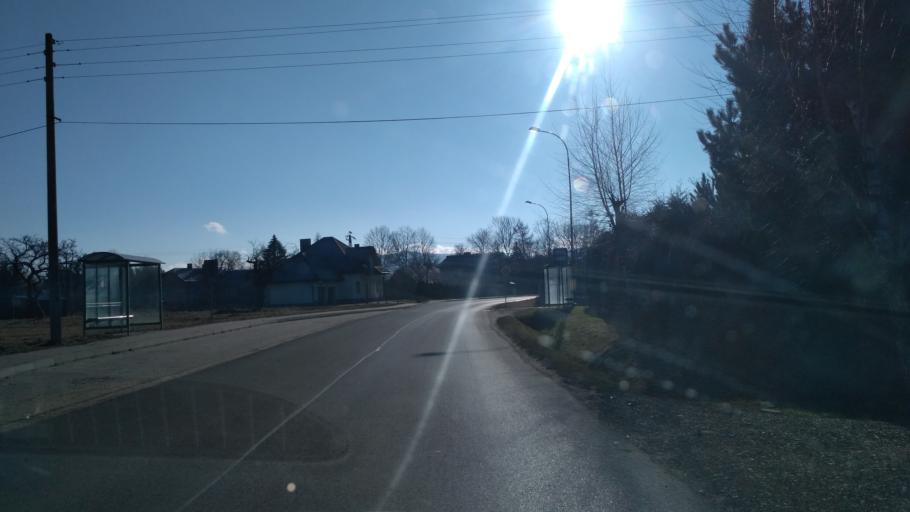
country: PL
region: Subcarpathian Voivodeship
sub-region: Powiat krosnienski
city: Rymanow
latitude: 49.5871
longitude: 21.8667
